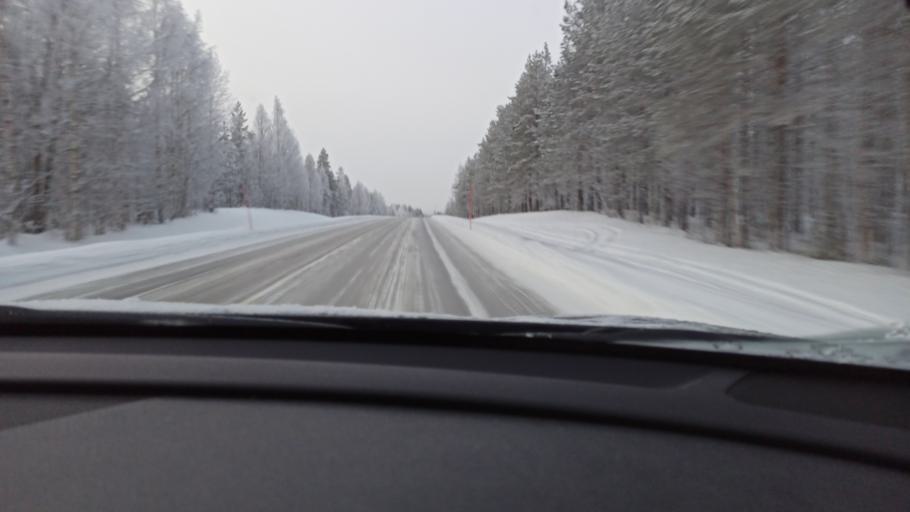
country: FI
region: Lapland
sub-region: Pohjois-Lappi
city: Sodankylae
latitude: 66.9340
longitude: 26.2671
